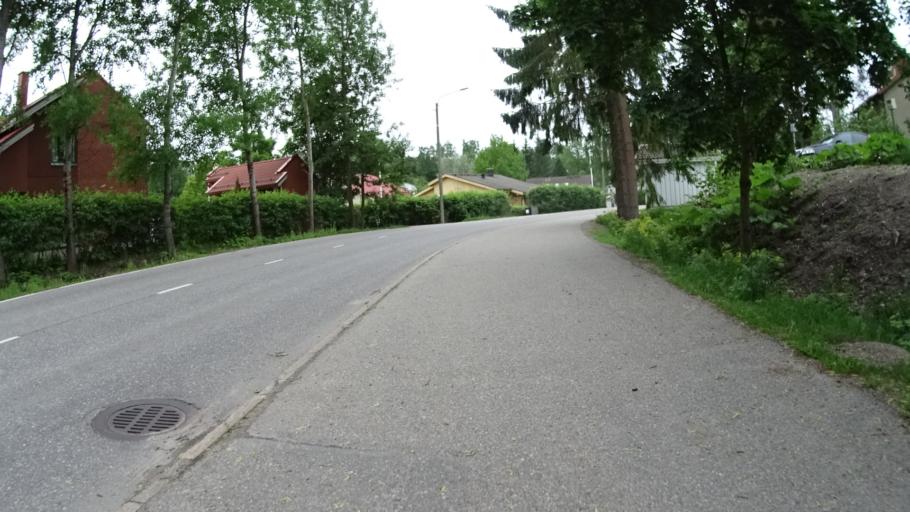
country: FI
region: Uusimaa
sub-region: Helsinki
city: Kilo
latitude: 60.2638
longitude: 24.8159
